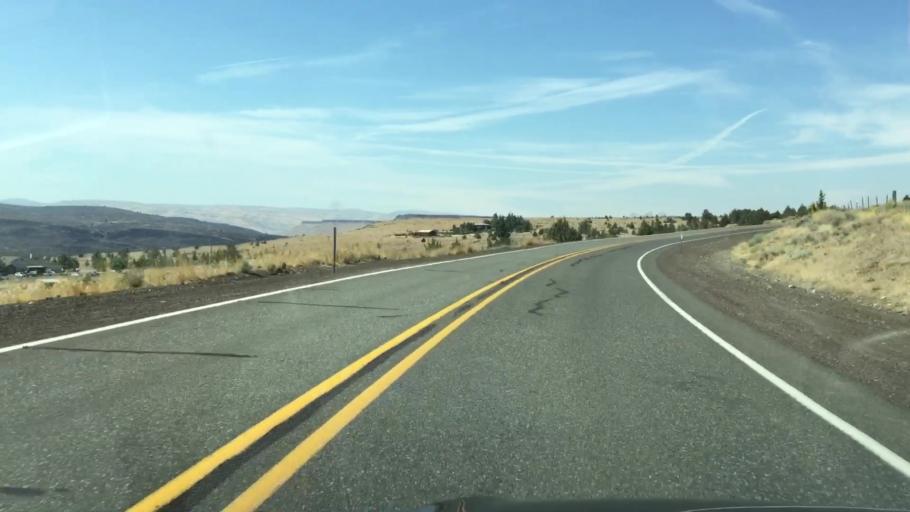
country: US
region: Oregon
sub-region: Wasco County
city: The Dalles
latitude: 45.1700
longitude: -121.0945
